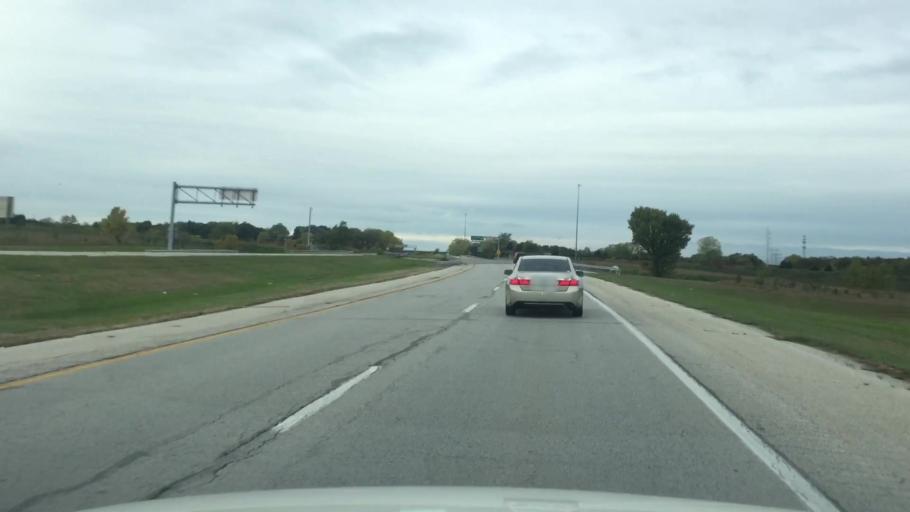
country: US
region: Kansas
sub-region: Wyandotte County
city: Edwardsville
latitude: 39.0107
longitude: -94.7827
